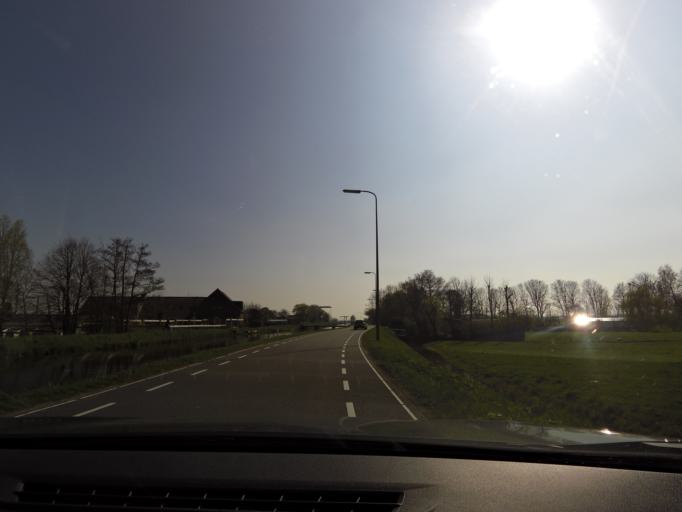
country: NL
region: South Holland
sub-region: Gemeente Westland
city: De Lier
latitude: 51.9665
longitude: 4.3036
